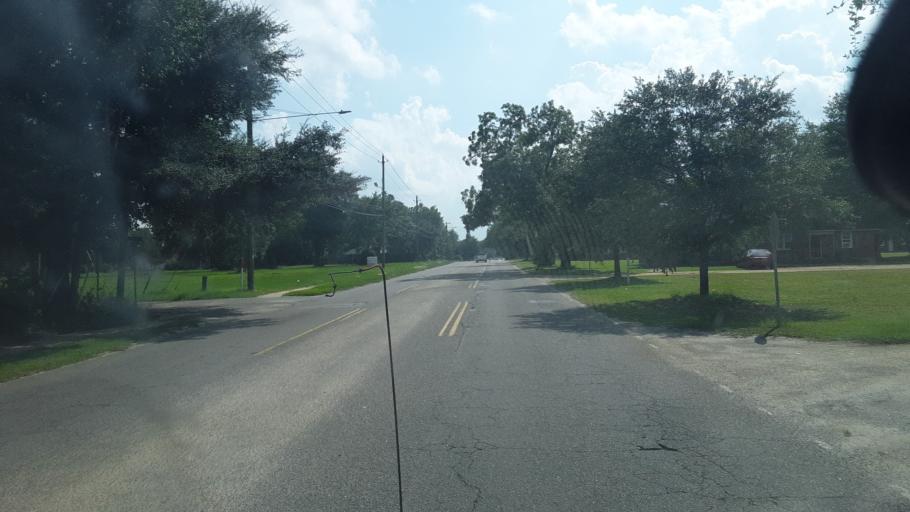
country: US
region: South Carolina
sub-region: Sumter County
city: Sumter
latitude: 33.9423
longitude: -80.3577
